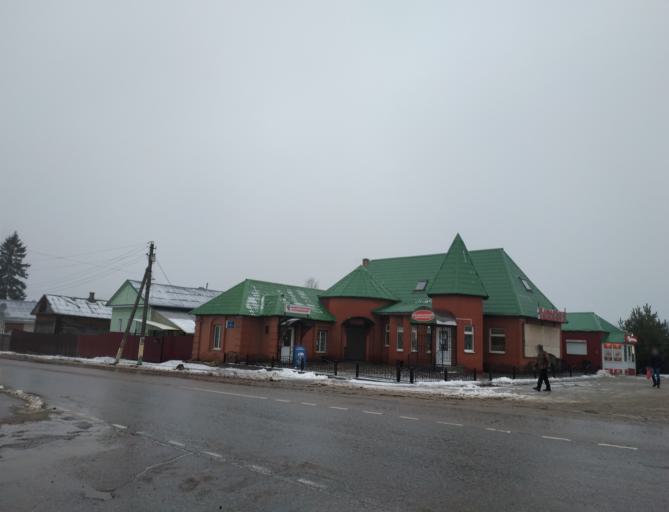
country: RU
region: Moskovskaya
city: Taldom
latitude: 56.7278
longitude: 37.5320
